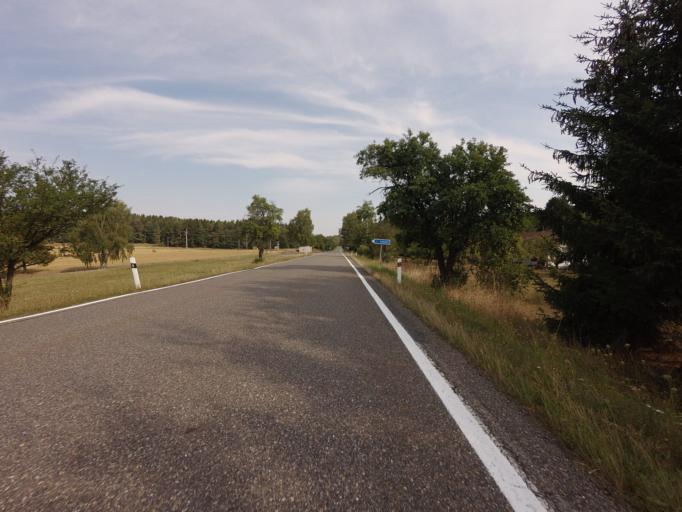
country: CZ
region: Central Bohemia
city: Petrovice
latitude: 49.5234
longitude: 14.3546
